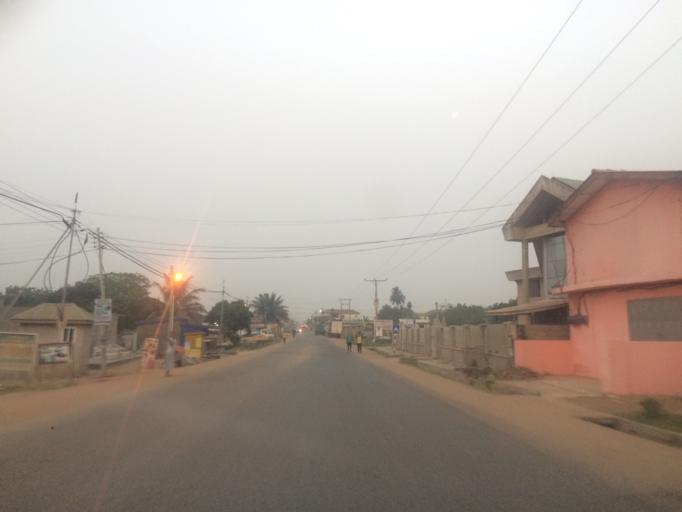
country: GH
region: Greater Accra
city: Teshi Old Town
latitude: 5.5915
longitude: -0.1015
